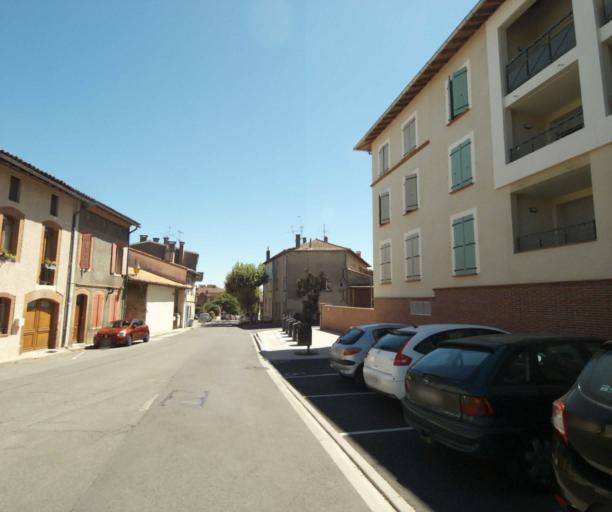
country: FR
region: Midi-Pyrenees
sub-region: Departement de la Haute-Garonne
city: Castanet-Tolosan
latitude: 43.5140
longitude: 1.4975
